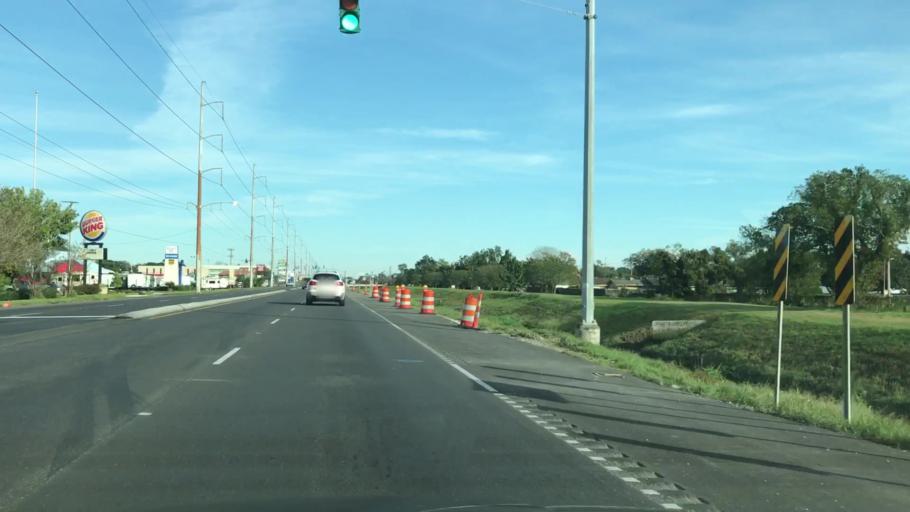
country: US
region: Louisiana
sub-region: Jefferson Parish
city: River Ridge
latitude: 29.9788
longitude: -90.2265
